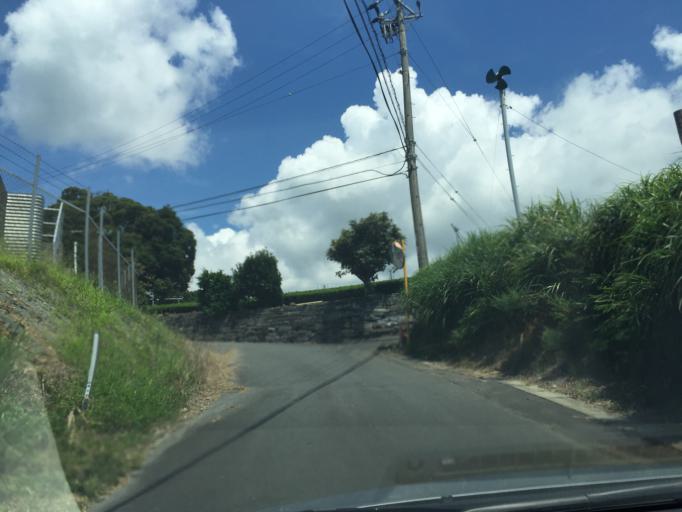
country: JP
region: Shizuoka
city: Kanaya
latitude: 34.8114
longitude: 138.0913
